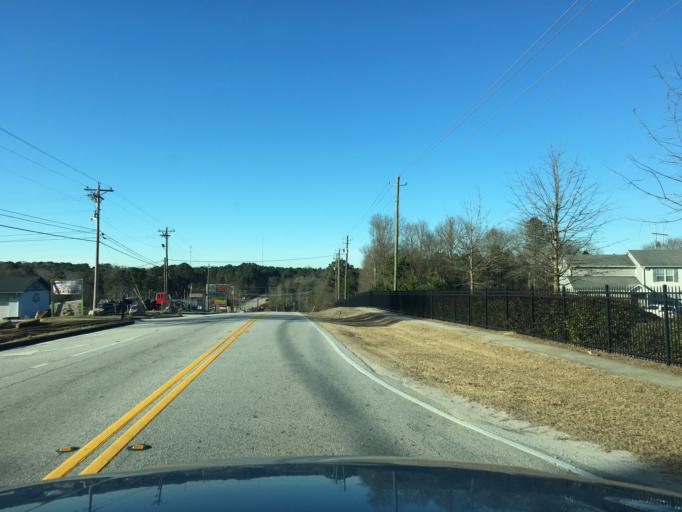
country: US
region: Georgia
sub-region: Rockdale County
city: Conyers
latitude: 33.6840
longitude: -84.0309
